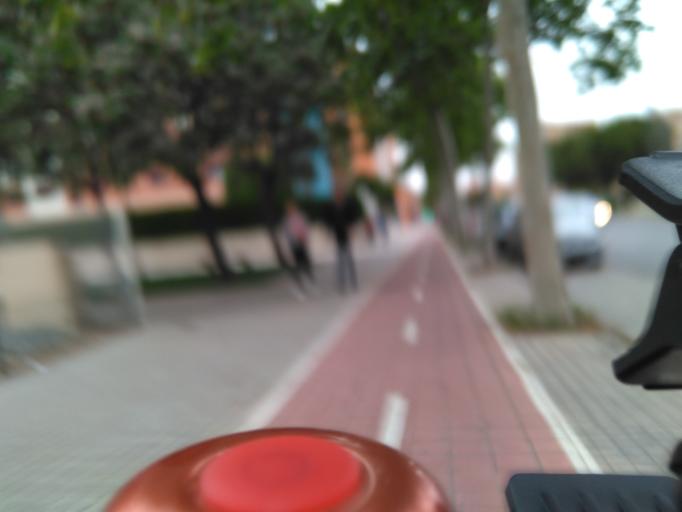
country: ES
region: Valencia
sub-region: Provincia de Valencia
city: Mislata
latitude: 39.4792
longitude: -0.3990
